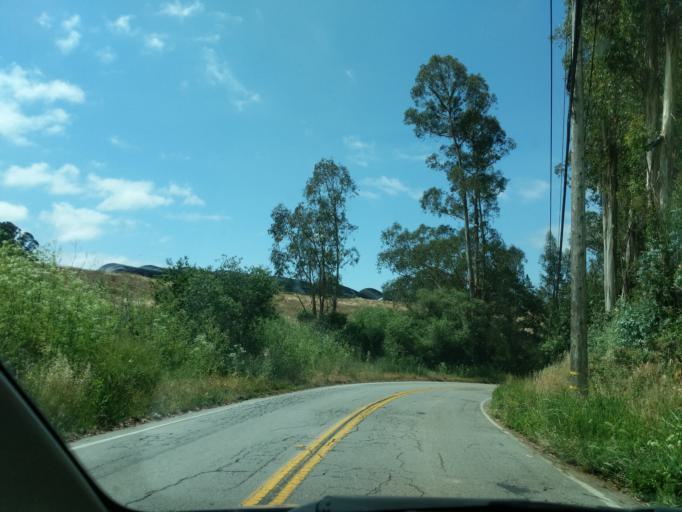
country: US
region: California
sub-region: Santa Cruz County
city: Freedom
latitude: 36.9395
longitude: -121.8034
